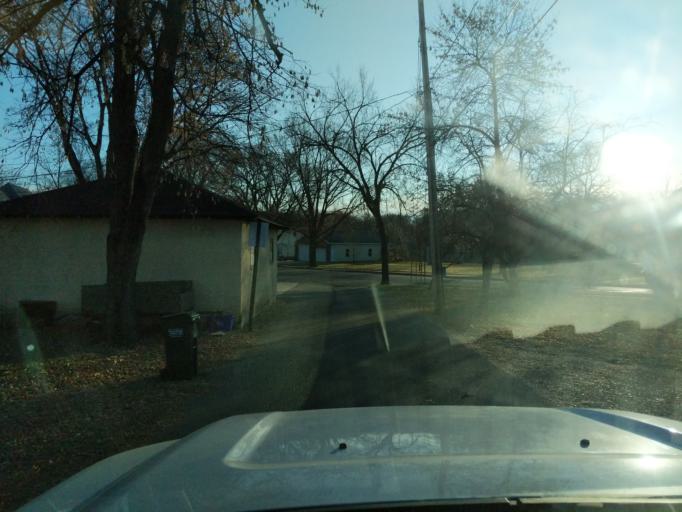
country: US
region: Minnesota
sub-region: Yellow Medicine County
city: Granite Falls
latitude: 44.8081
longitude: -95.5415
